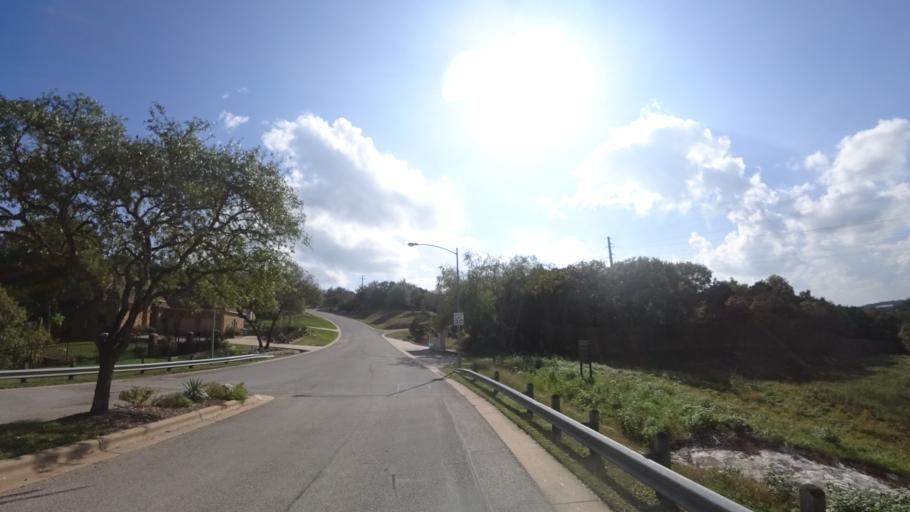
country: US
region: Texas
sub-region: Travis County
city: Lost Creek
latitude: 30.3118
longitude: -97.8535
